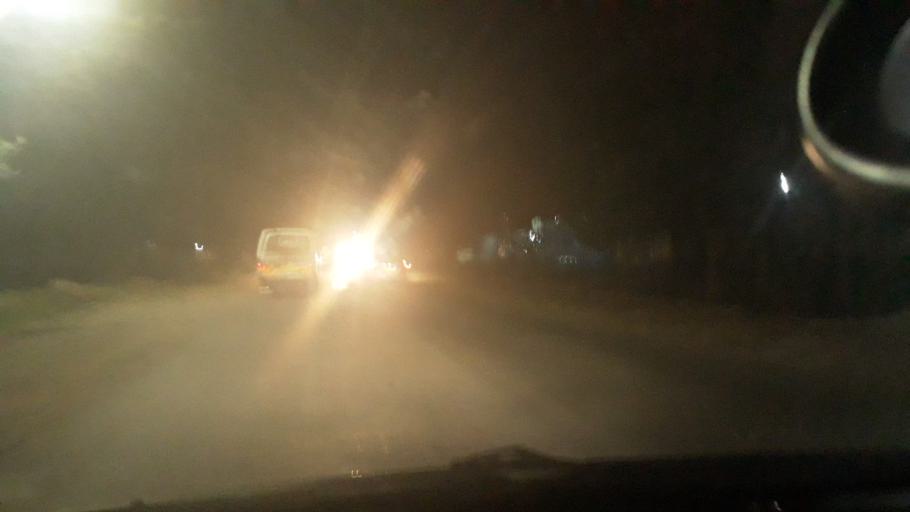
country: KE
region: Nairobi Area
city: Pumwani
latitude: -1.2625
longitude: 36.9073
